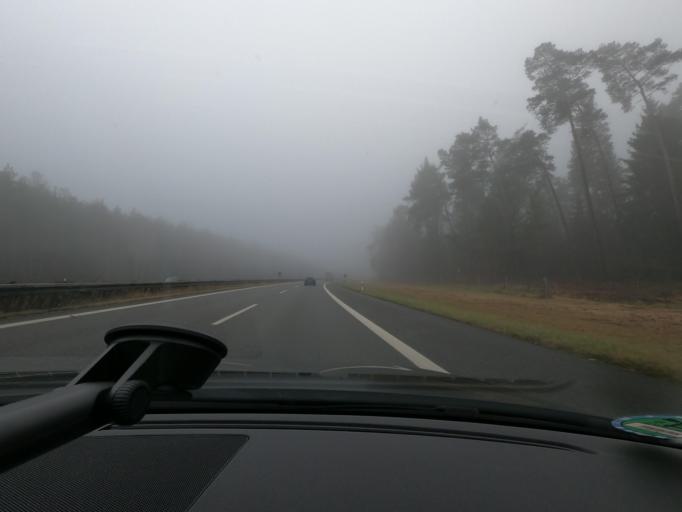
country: DE
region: Bavaria
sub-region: Regierungsbezirk Mittelfranken
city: Rothenbach an der Pegnitz
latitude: 49.4595
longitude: 11.2366
